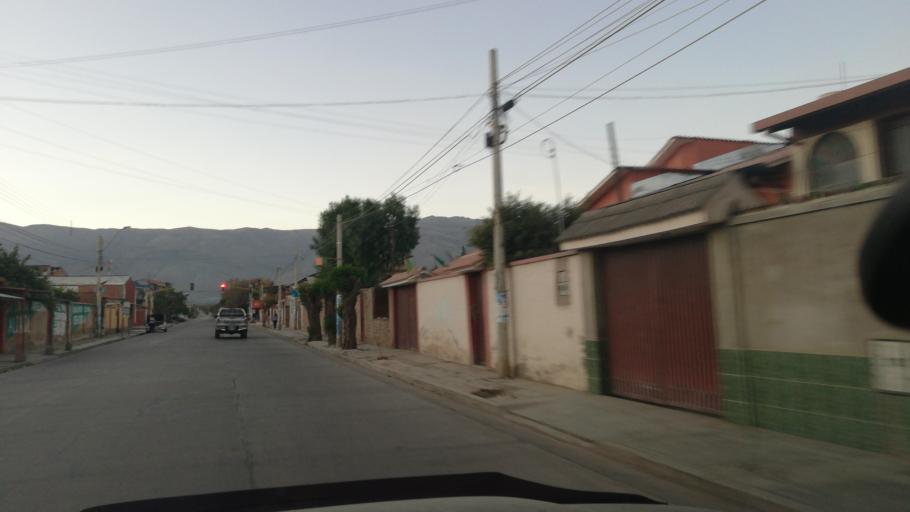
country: BO
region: Cochabamba
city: Cochabamba
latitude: -17.3891
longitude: -66.2192
